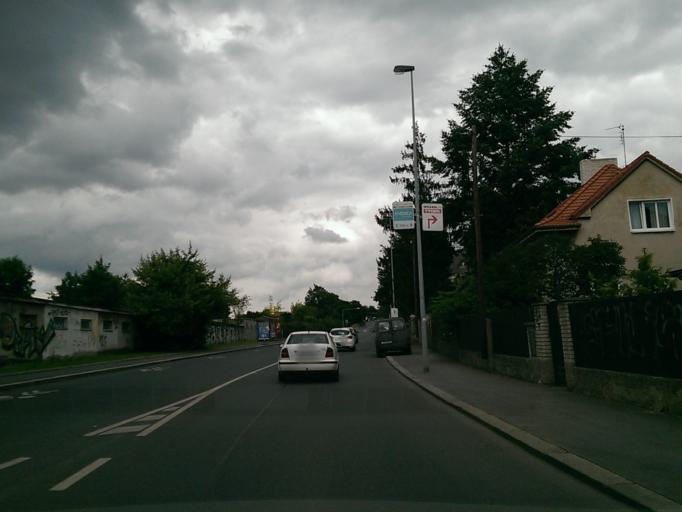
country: CZ
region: Praha
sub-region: Praha 4
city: Hodkovicky
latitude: 50.0313
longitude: 14.4204
